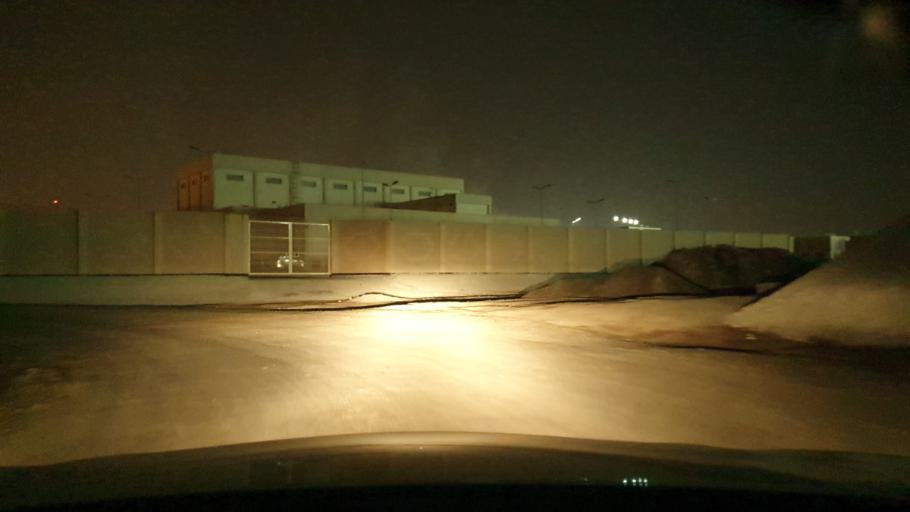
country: BH
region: Northern
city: Sitrah
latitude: 26.0958
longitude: 50.6114
